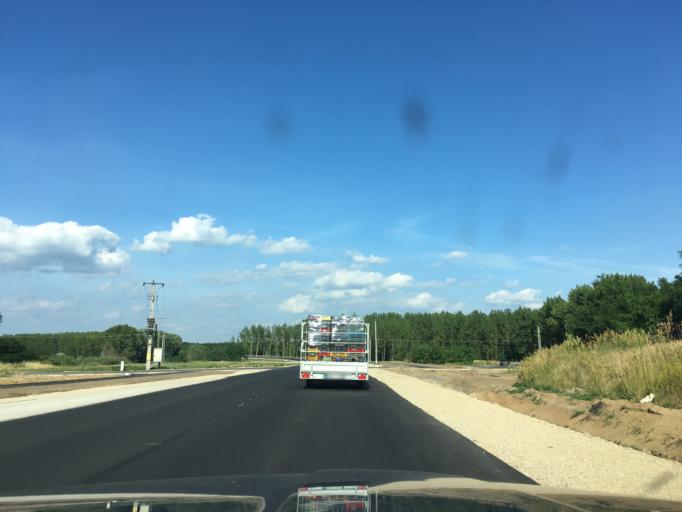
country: HU
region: Hajdu-Bihar
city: Hajdusamson
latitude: 47.6441
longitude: 21.8231
